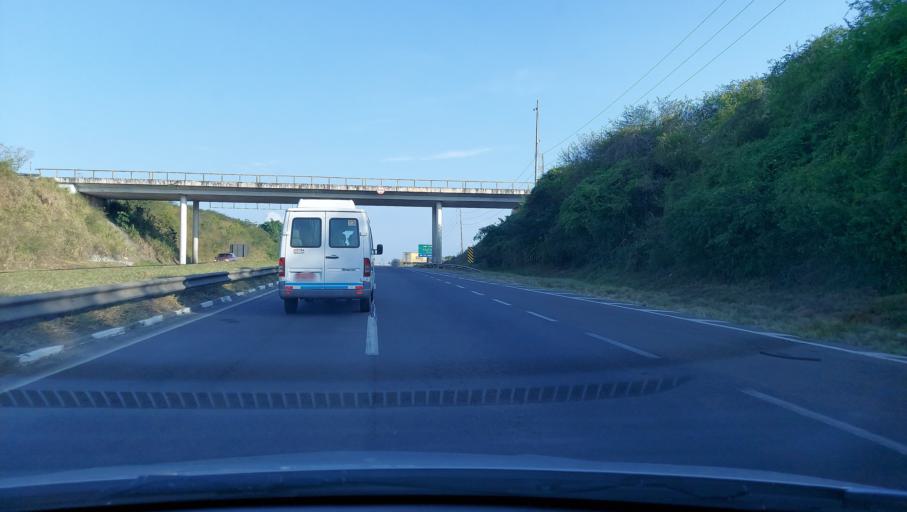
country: BR
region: Bahia
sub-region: Conceicao Do Jacuipe
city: Conceicao do Jacuipe
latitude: -12.3597
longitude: -38.8260
